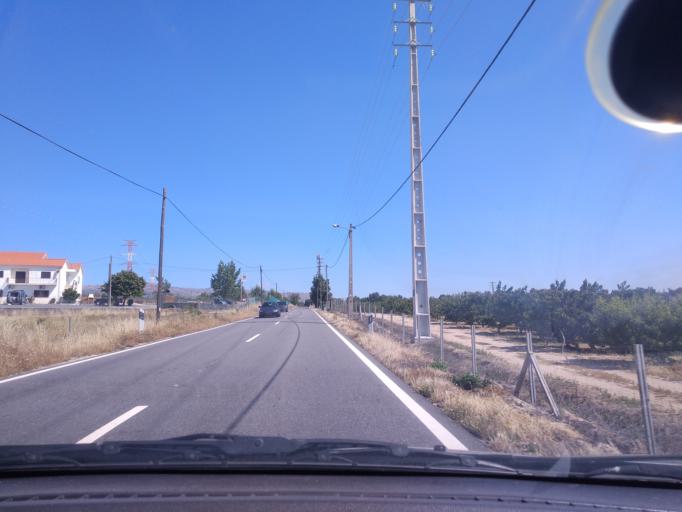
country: PT
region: Guarda
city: Alcains
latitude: 39.9785
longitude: -7.4565
